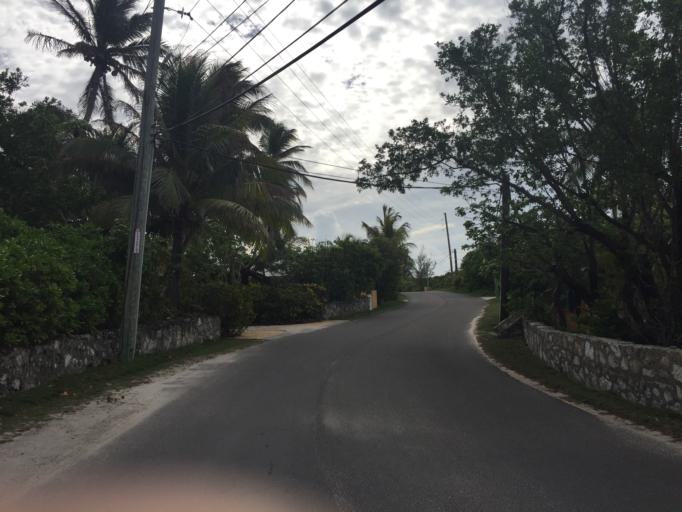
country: BS
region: Central Abaco
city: Marsh Harbour
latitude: 26.5300
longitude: -76.9614
